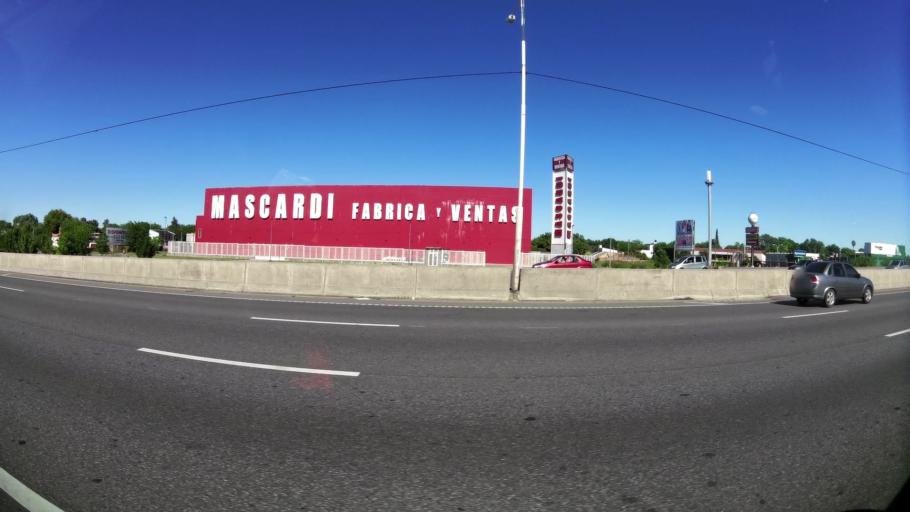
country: AR
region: Santa Fe
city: Granadero Baigorria
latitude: -32.9337
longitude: -60.7228
